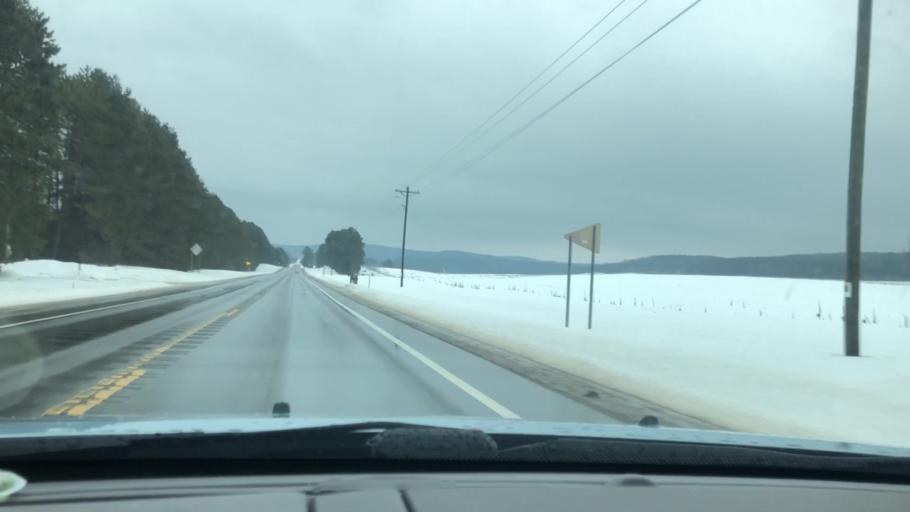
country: US
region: Michigan
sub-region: Charlevoix County
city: Boyne City
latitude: 45.0945
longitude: -84.9726
